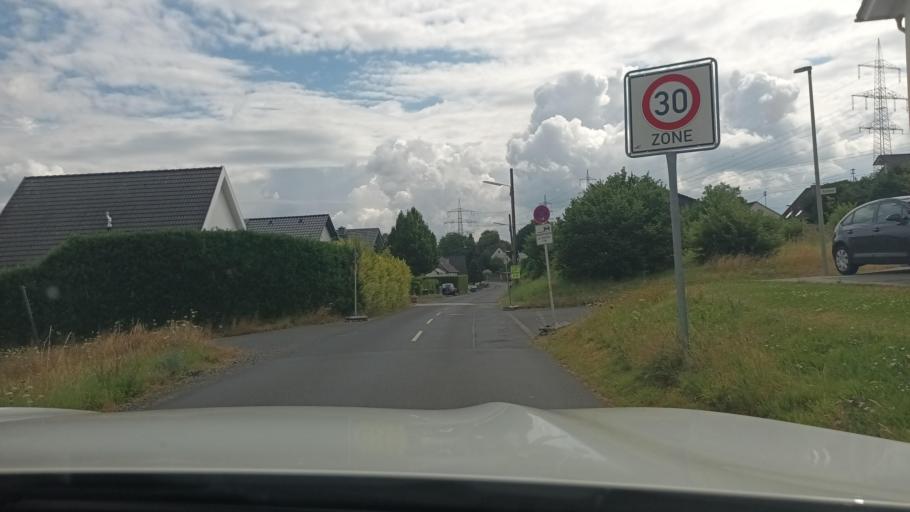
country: DE
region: North Rhine-Westphalia
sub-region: Regierungsbezirk Koln
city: Eitorf
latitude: 50.7555
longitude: 7.4226
